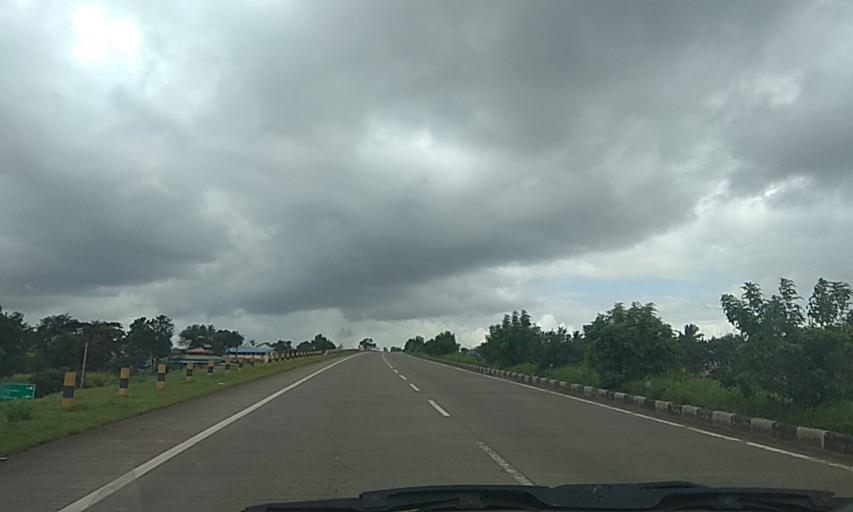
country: IN
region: Karnataka
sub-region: Belgaum
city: Sankeshwar
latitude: 16.2543
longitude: 74.4715
